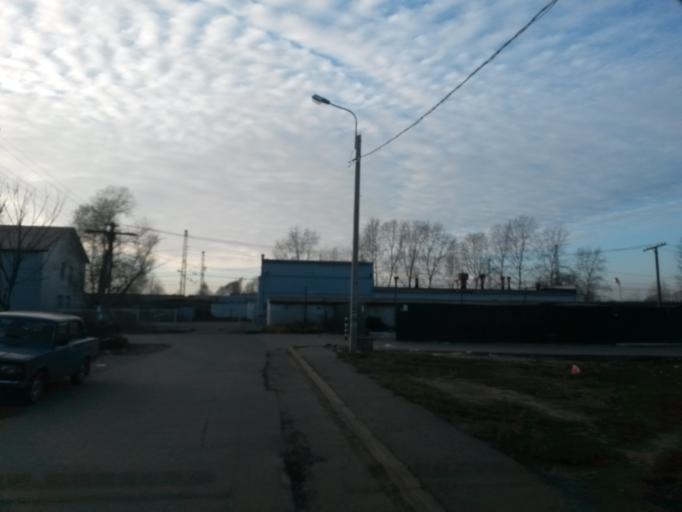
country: RU
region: Moskovskaya
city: Stolbovaya
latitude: 55.2506
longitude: 37.4962
